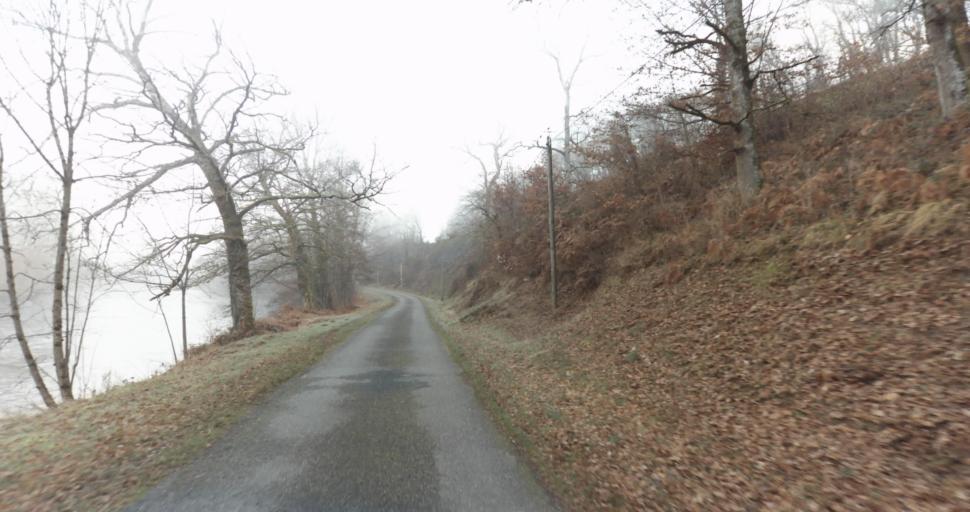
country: FR
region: Limousin
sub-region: Departement de la Haute-Vienne
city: Saint-Priest-sous-Aixe
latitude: 45.8163
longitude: 1.1197
